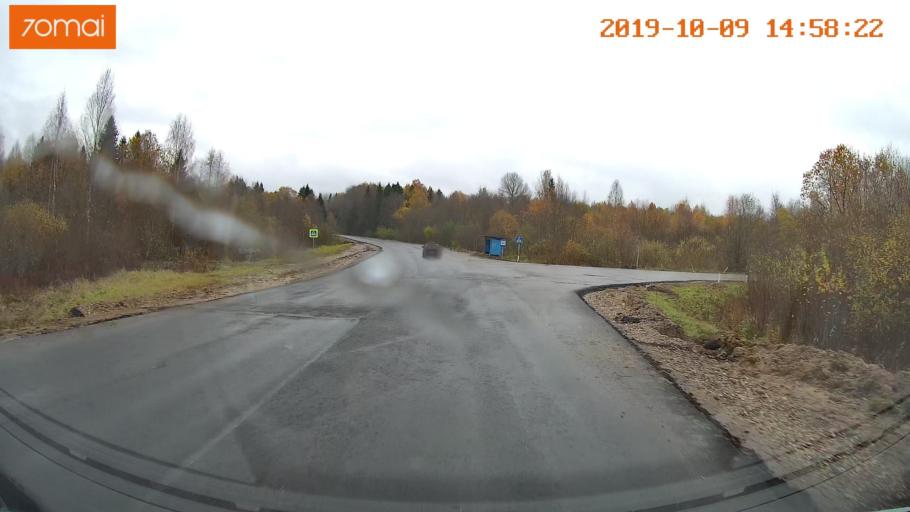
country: RU
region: Kostroma
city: Chistyye Bory
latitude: 58.3275
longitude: 41.6545
